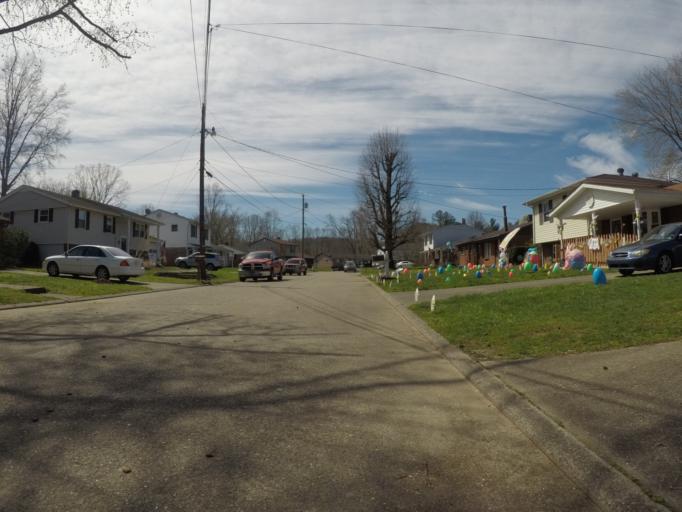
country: US
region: West Virginia
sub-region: Cabell County
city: Pea Ridge
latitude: 38.3981
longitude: -82.3157
